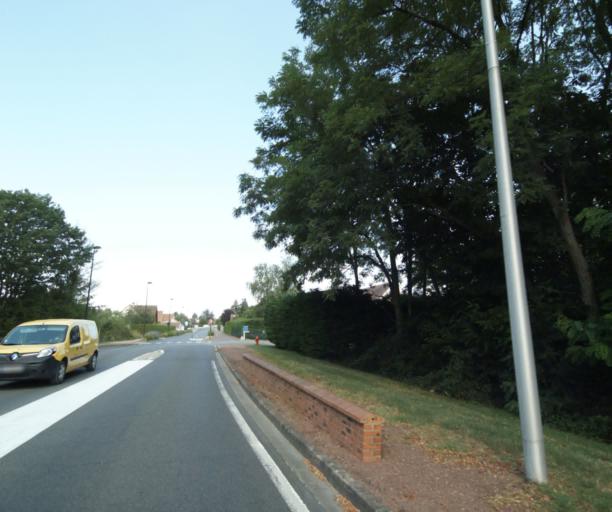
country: FR
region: Centre
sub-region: Departement du Loiret
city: Saint-Cyr-en-Val
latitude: 47.8239
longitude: 1.9792
